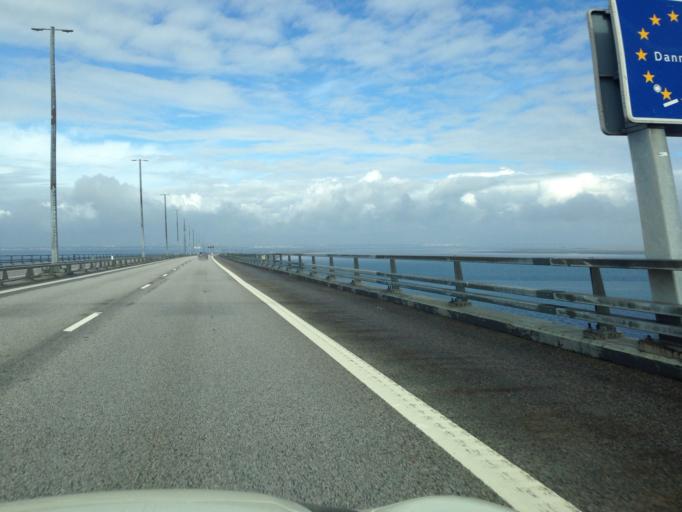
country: DK
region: Capital Region
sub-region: Dragor Kommune
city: Dragor
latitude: 55.5794
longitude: 12.8088
